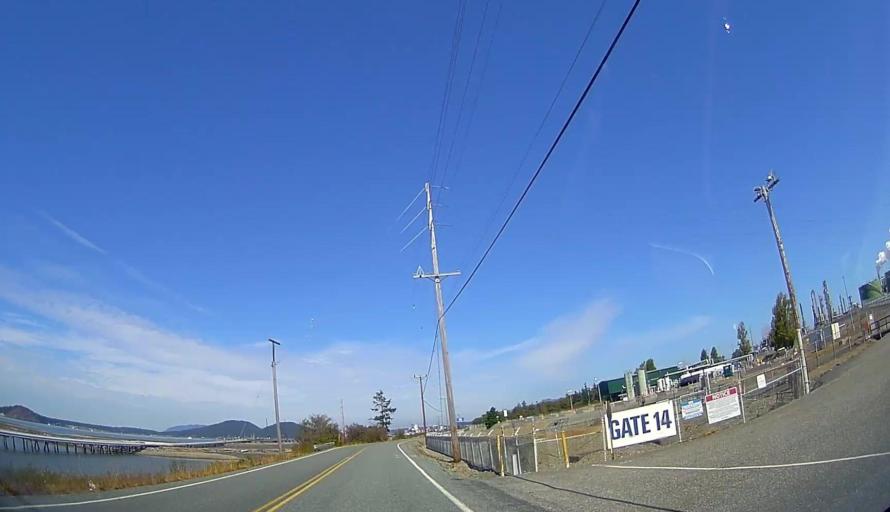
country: US
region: Washington
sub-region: Skagit County
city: Anacortes
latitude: 48.4909
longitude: -122.5751
